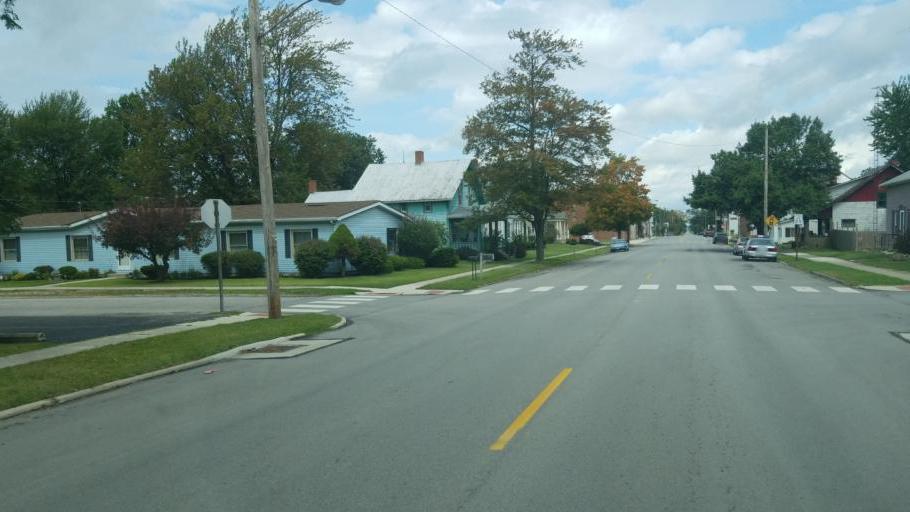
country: US
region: Ohio
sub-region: Seneca County
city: Tiffin
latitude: 41.0502
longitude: -83.0154
